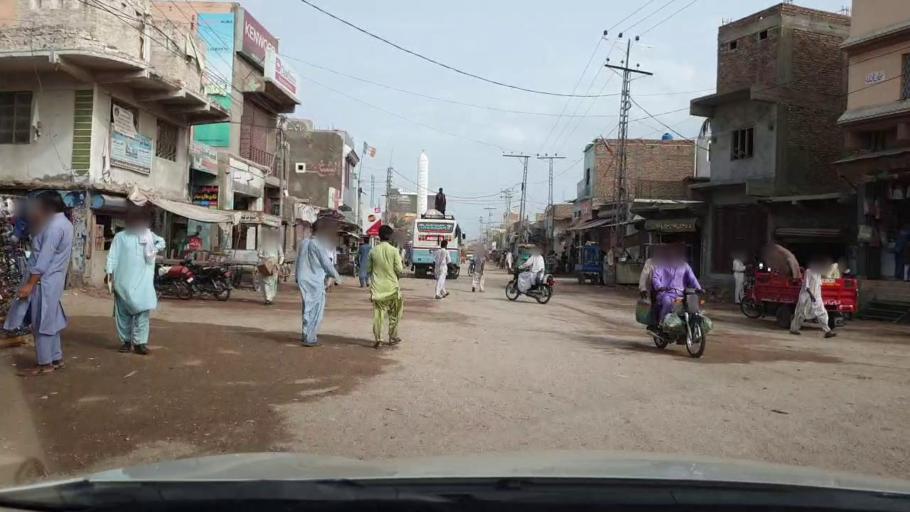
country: PK
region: Sindh
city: Matli
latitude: 25.0427
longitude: 68.6589
